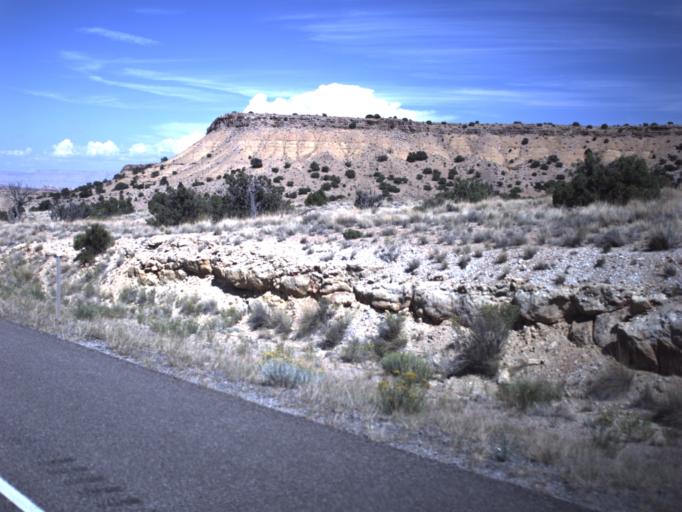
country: US
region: Utah
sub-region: Emery County
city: Castle Dale
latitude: 38.9199
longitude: -110.5009
